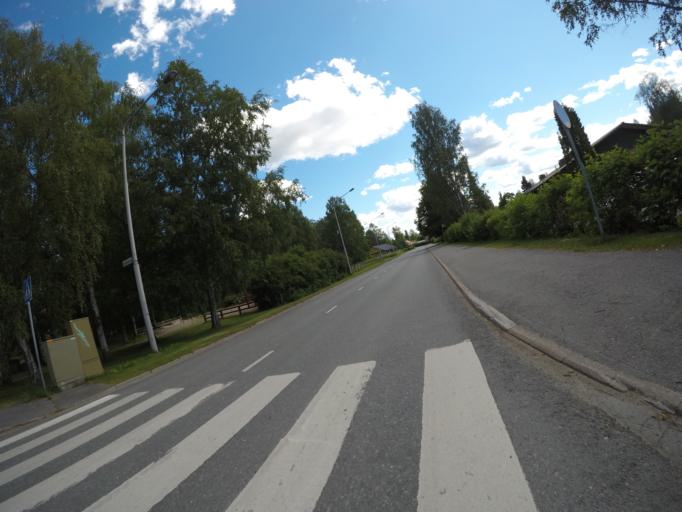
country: FI
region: Haeme
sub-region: Haemeenlinna
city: Haemeenlinna
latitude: 61.0139
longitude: 24.4283
